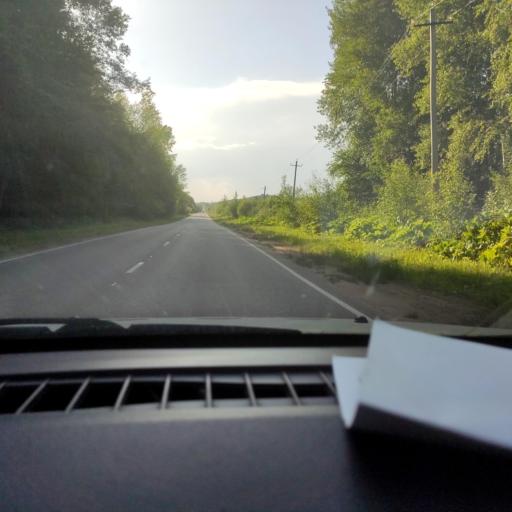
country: RU
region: Perm
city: Krasnokamsk
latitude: 58.1253
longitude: 55.8038
